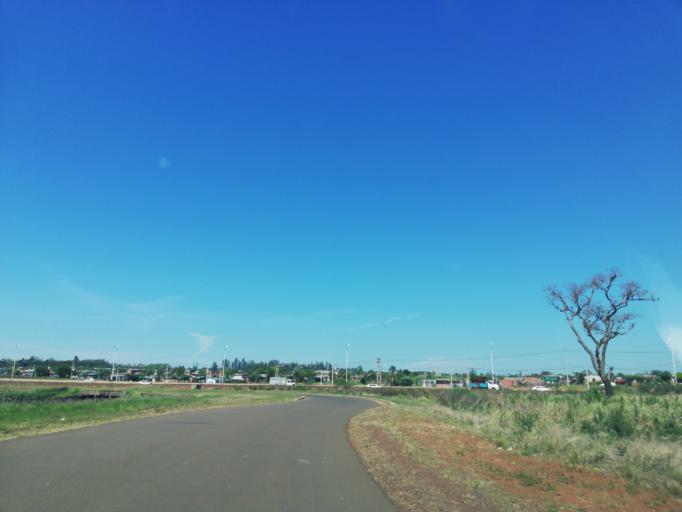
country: AR
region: Misiones
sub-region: Departamento de Capital
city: Posadas
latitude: -27.4275
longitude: -55.8695
